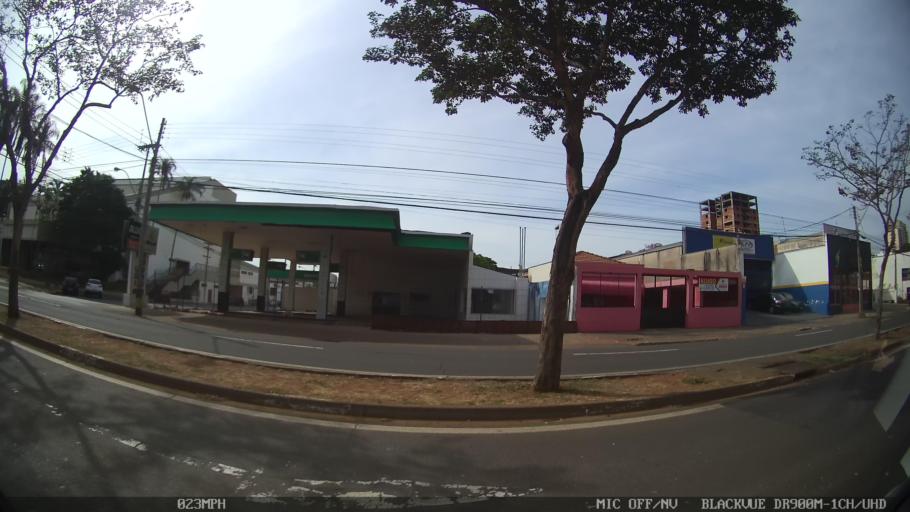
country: BR
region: Sao Paulo
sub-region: Piracicaba
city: Piracicaba
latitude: -22.7350
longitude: -47.6490
